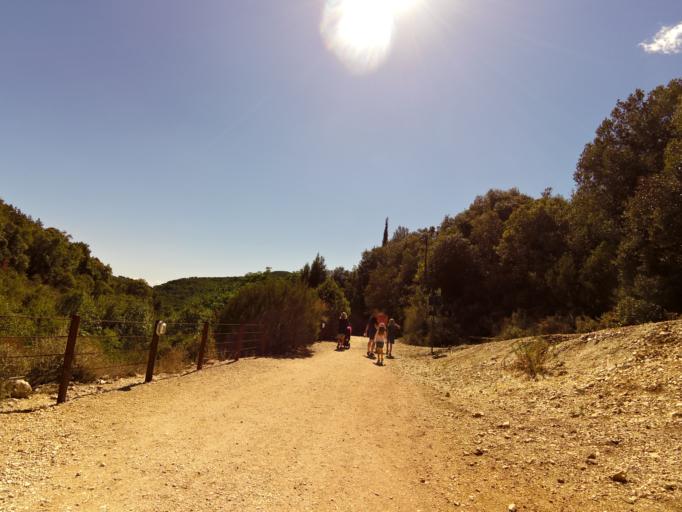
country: IT
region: Tuscany
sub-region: Provincia di Livorno
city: Campiglia Marittima
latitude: 43.0770
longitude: 10.6148
